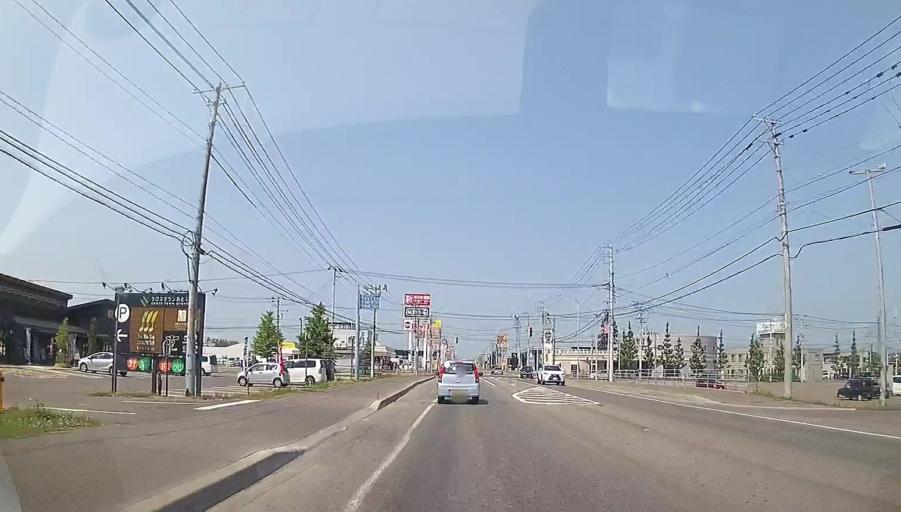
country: JP
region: Hokkaido
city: Otofuke
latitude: 42.9614
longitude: 143.2064
